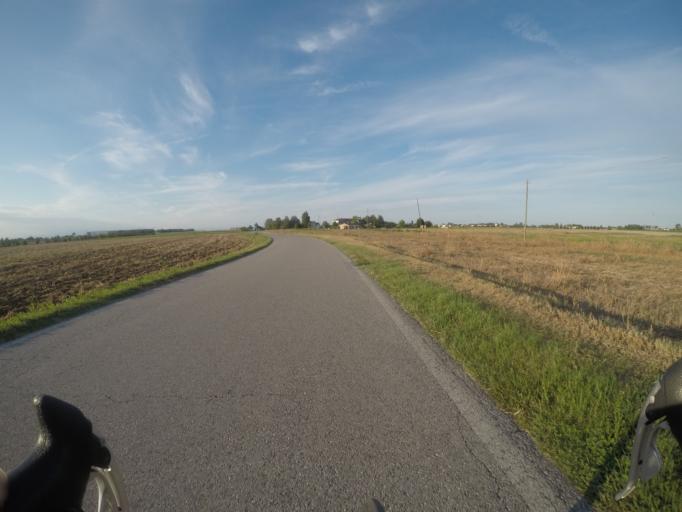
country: IT
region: Veneto
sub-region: Provincia di Rovigo
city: San Bellino
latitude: 45.0194
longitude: 11.5725
